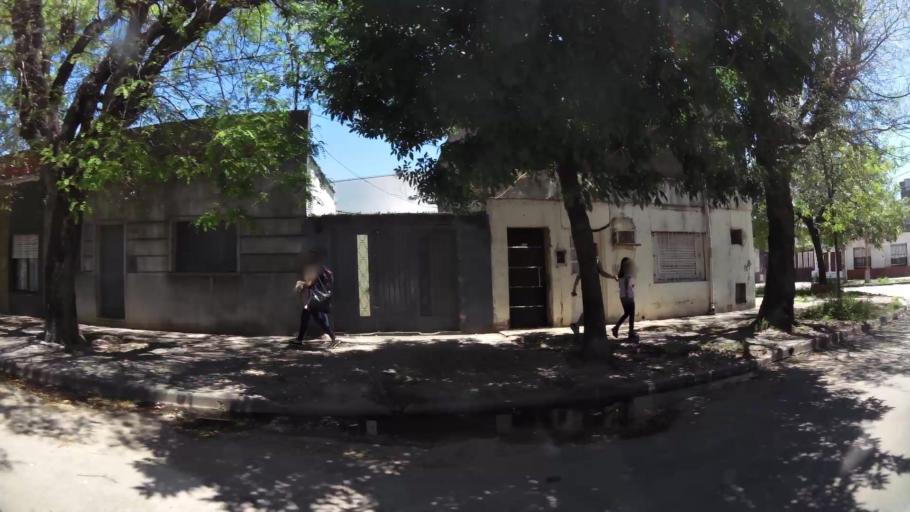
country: AR
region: Santa Fe
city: Santa Fe de la Vera Cruz
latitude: -31.6494
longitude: -60.7268
